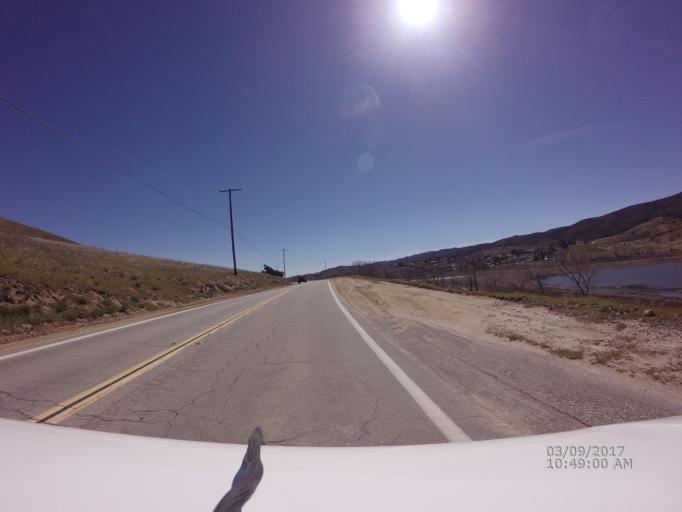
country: US
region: California
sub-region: Los Angeles County
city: Green Valley
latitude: 34.6687
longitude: -118.4046
